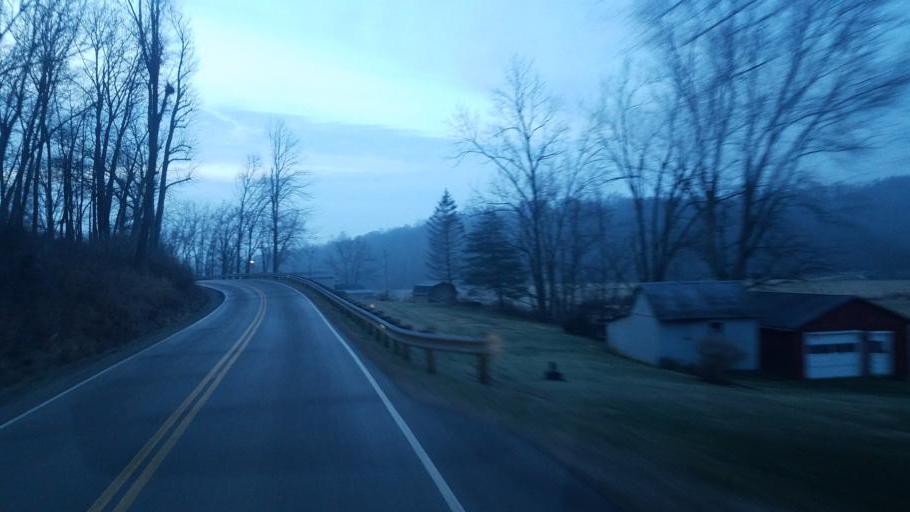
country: US
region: Ohio
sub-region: Coshocton County
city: West Lafayette
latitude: 40.3391
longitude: -81.7495
